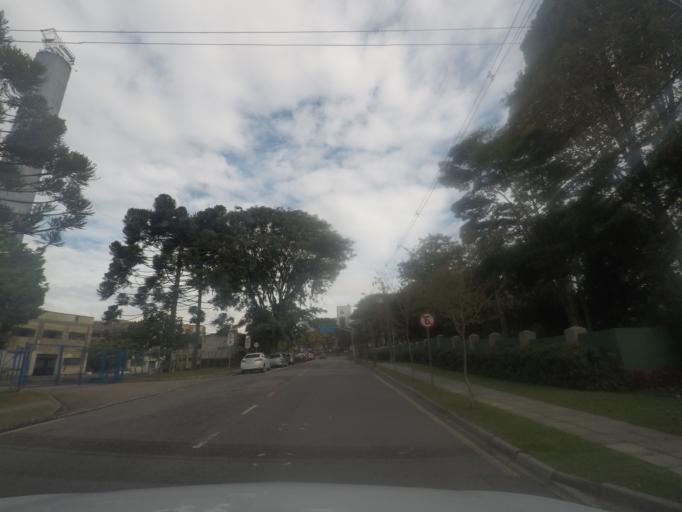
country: BR
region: Parana
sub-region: Curitiba
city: Curitiba
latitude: -25.4344
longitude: -49.2458
